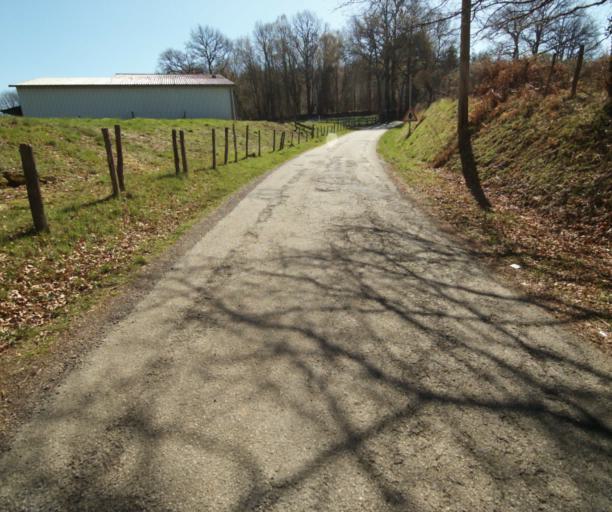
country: FR
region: Limousin
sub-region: Departement de la Correze
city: Seilhac
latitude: 45.3617
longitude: 1.7192
